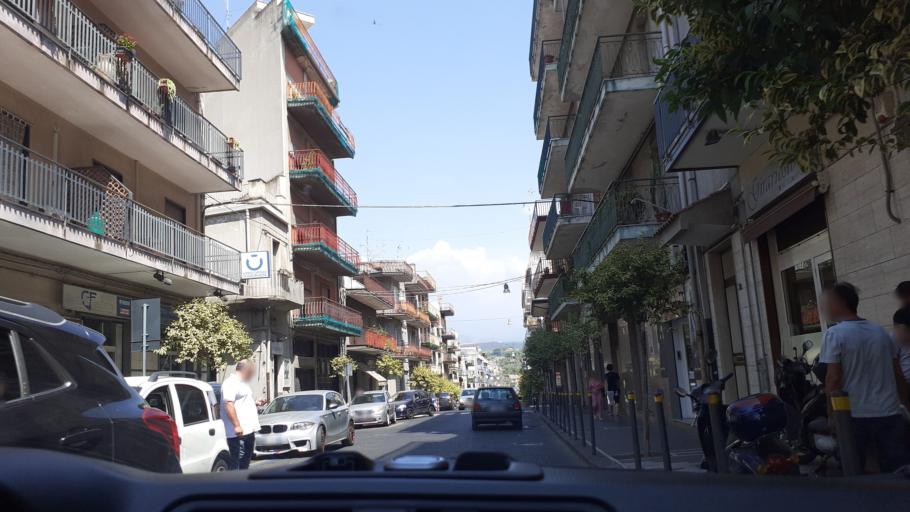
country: IT
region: Sicily
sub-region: Catania
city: Belvedere-Piano Tavola
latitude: 37.5193
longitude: 15.0072
